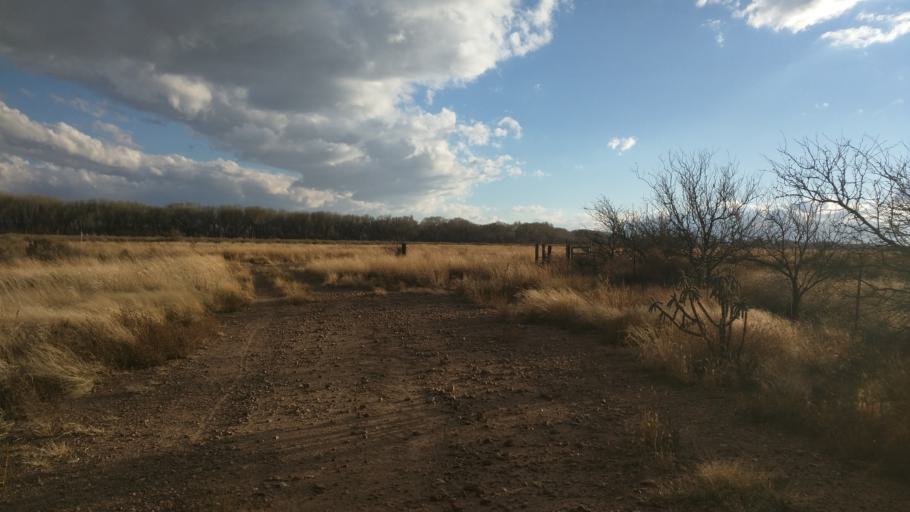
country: US
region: Arizona
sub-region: Cochise County
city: Sierra Vista Southeast
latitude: 31.3695
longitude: -110.1223
